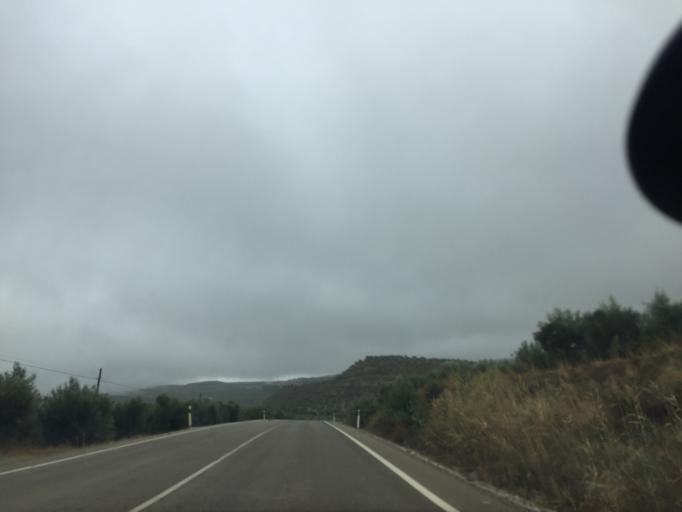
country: ES
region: Andalusia
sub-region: Provincia de Jaen
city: Torres
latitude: 37.8336
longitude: -3.5543
